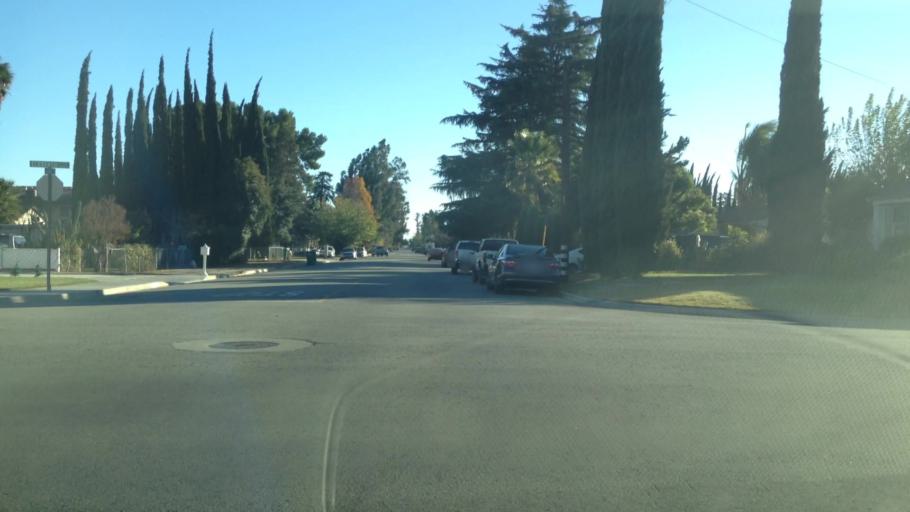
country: US
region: California
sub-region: Riverside County
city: Beaumont
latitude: 33.9372
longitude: -116.9801
